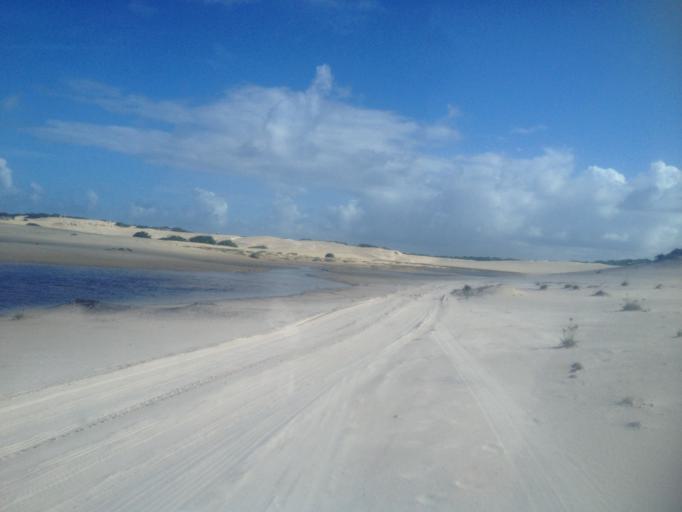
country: BR
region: Sergipe
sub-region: Indiaroba
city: Indiaroba
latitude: -11.4746
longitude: -37.3725
